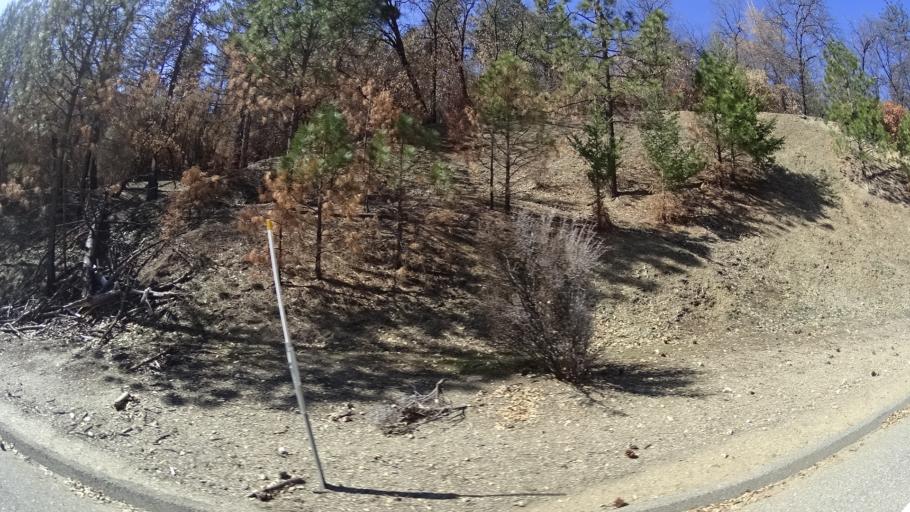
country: US
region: California
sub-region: Tehama County
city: Rancho Tehama Reserve
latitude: 39.6766
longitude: -122.7032
